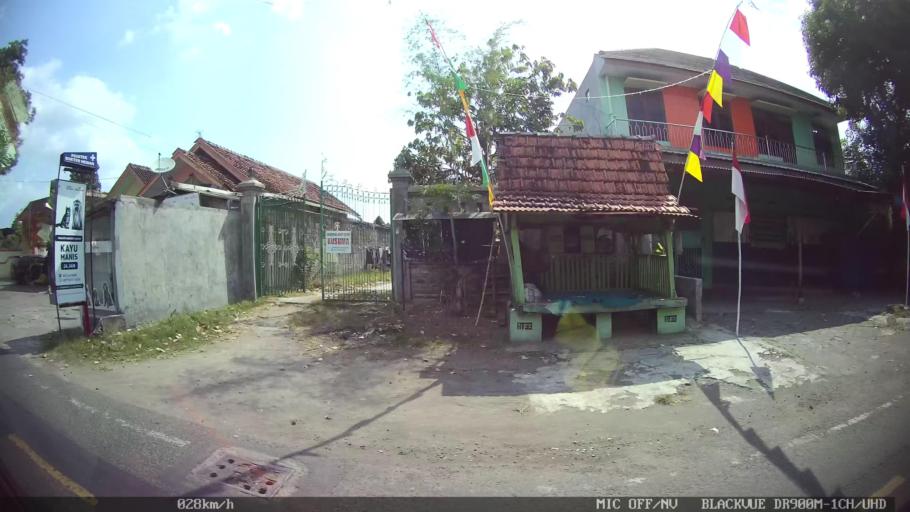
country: ID
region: Daerah Istimewa Yogyakarta
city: Yogyakarta
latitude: -7.8194
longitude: 110.3906
